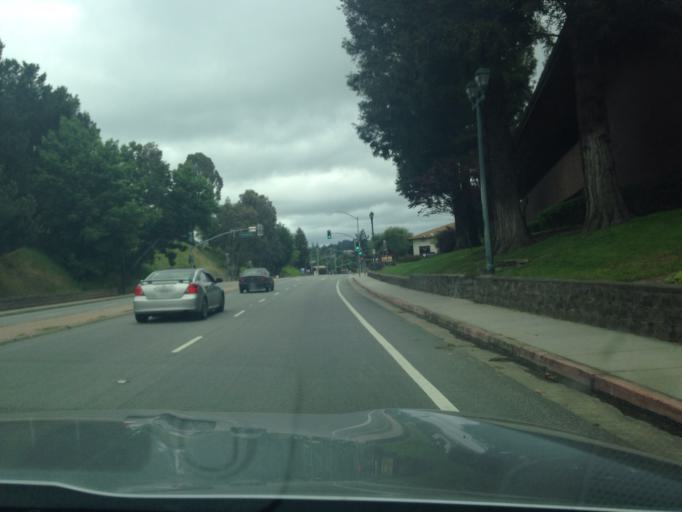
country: US
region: California
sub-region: Santa Cruz County
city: Scotts Valley
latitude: 37.0608
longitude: -122.0084
